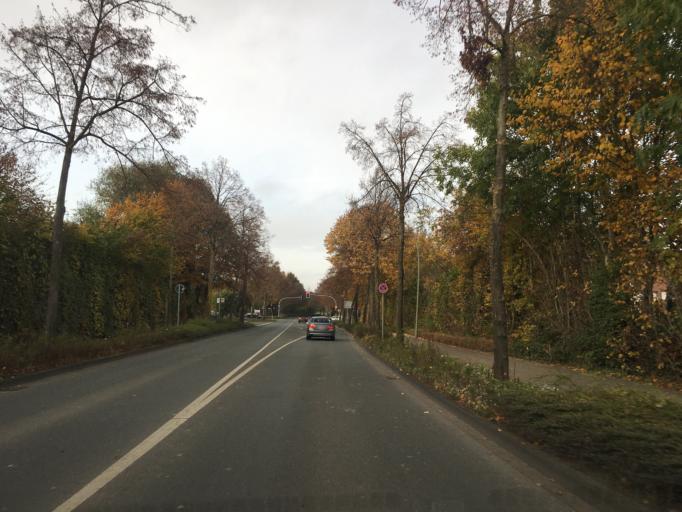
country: DE
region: North Rhine-Westphalia
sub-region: Regierungsbezirk Munster
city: Steinfurt
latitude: 52.1238
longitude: 7.3901
